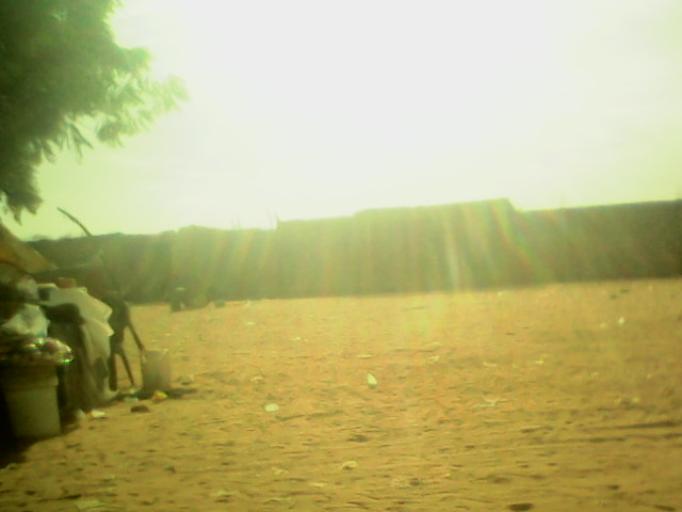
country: SN
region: Diourbel
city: Touba
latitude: 14.8587
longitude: -15.8948
